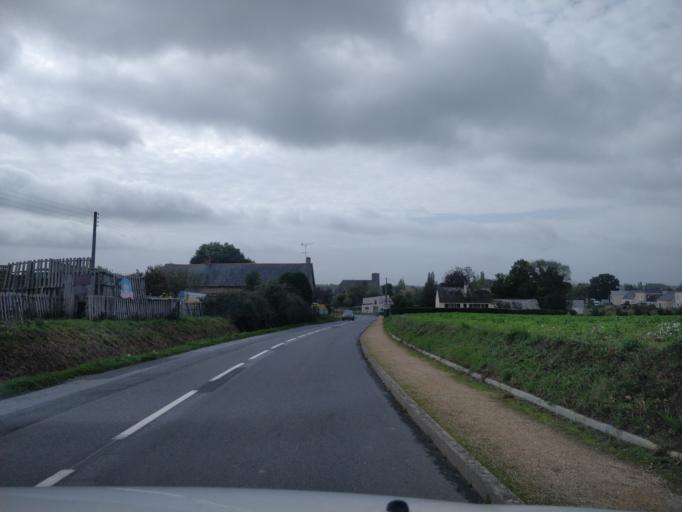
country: FR
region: Brittany
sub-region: Departement d'Ille-et-Vilaine
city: Servon-sur-Vilaine
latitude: 48.1269
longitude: -1.4585
